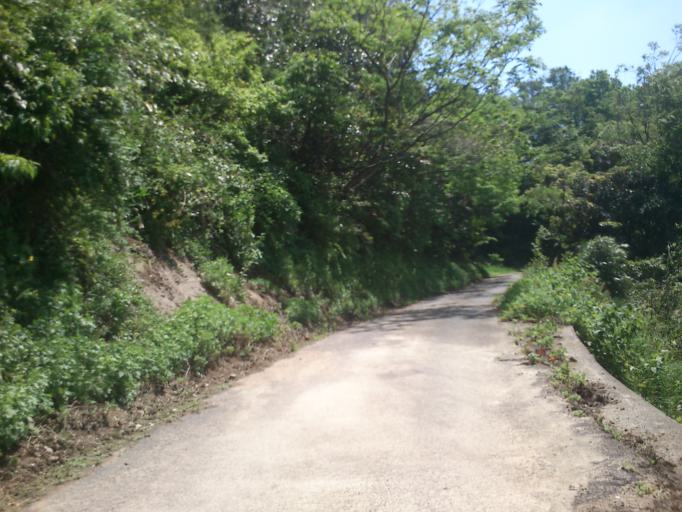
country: JP
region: Kyoto
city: Miyazu
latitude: 35.7168
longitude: 135.1375
